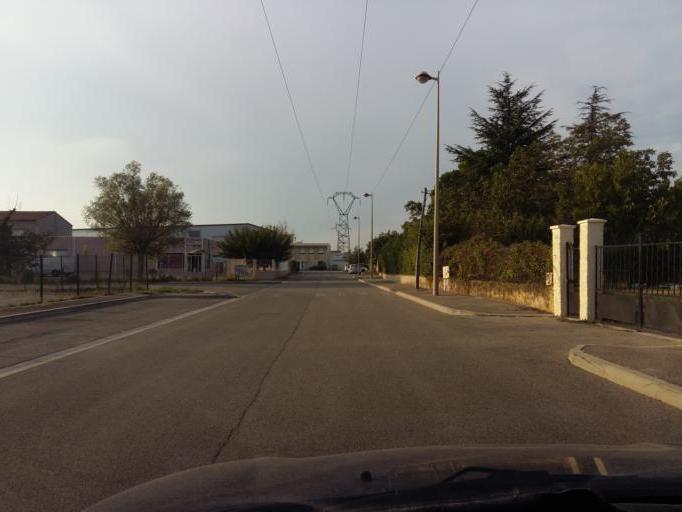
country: FR
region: Provence-Alpes-Cote d'Azur
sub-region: Departement du Vaucluse
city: Monteux
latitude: 44.0312
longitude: 4.9786
